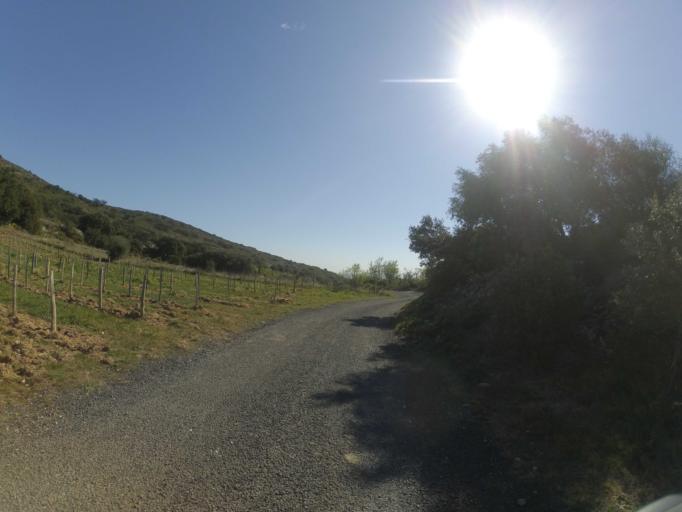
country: FR
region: Languedoc-Roussillon
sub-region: Departement des Pyrenees-Orientales
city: Baixas
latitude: 42.7619
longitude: 2.7624
